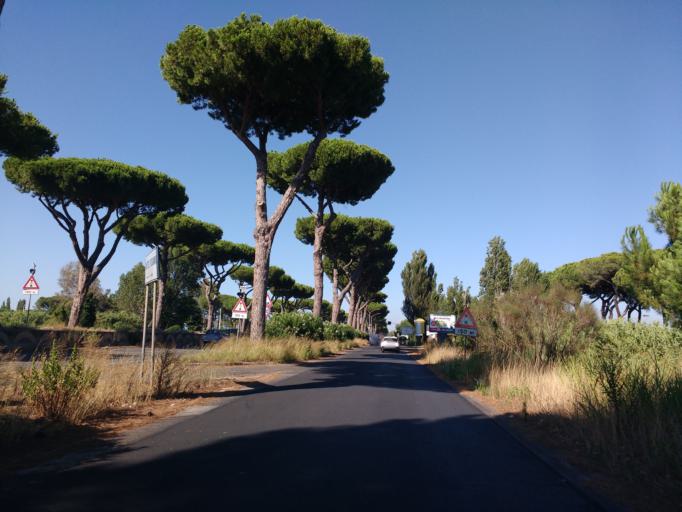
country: IT
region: Latium
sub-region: Citta metropolitana di Roma Capitale
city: Acilia-Castel Fusano-Ostia Antica
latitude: 41.7352
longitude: 12.3444
